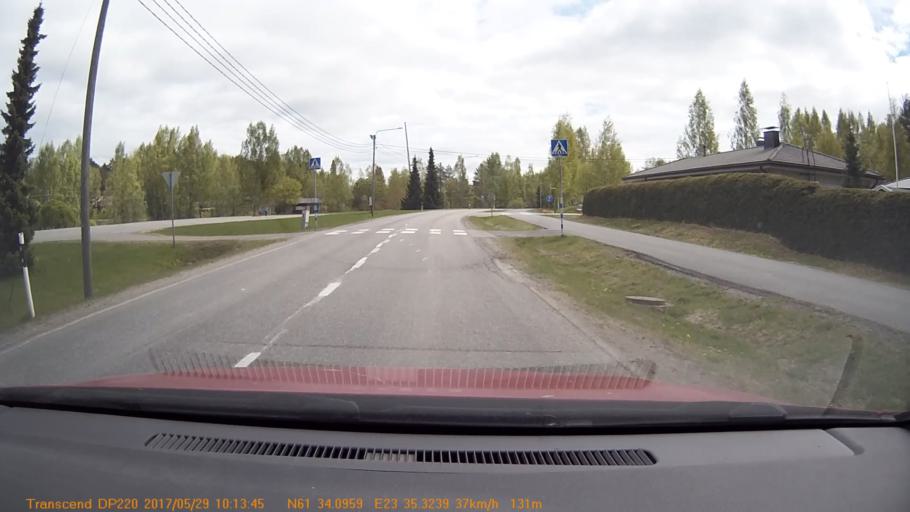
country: FI
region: Pirkanmaa
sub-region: Tampere
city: Yloejaervi
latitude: 61.5683
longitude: 23.5887
